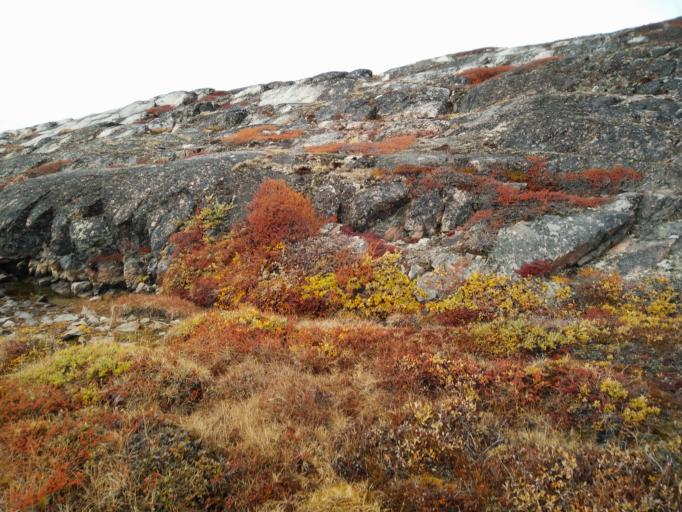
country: GL
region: Qaasuitsup
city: Ilulissat
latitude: 69.1992
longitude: -51.0731
